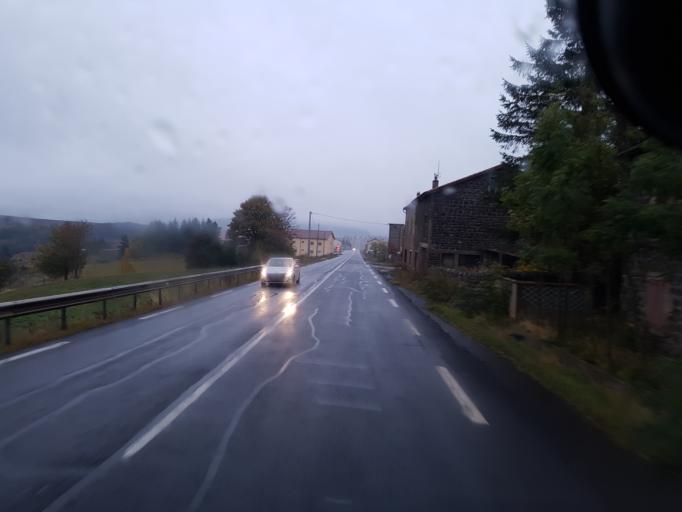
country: FR
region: Auvergne
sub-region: Departement de la Haute-Loire
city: Solignac-sur-Loire
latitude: 44.8507
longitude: 3.8498
